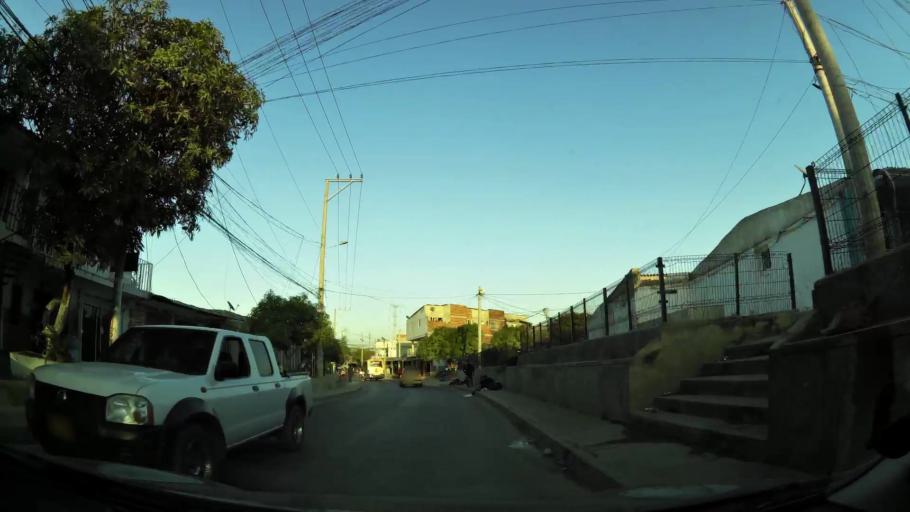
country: CO
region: Atlantico
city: Soledad
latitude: 10.9212
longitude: -74.7919
